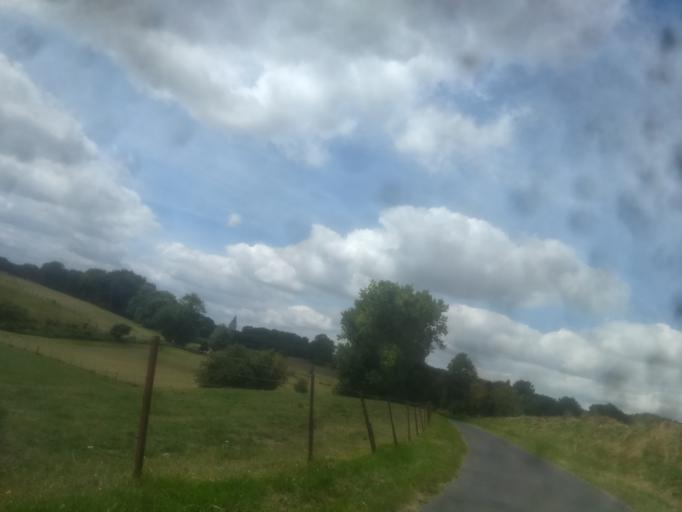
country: FR
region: Nord-Pas-de-Calais
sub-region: Departement du Pas-de-Calais
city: Beaumetz-les-Loges
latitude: 50.2268
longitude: 2.6540
